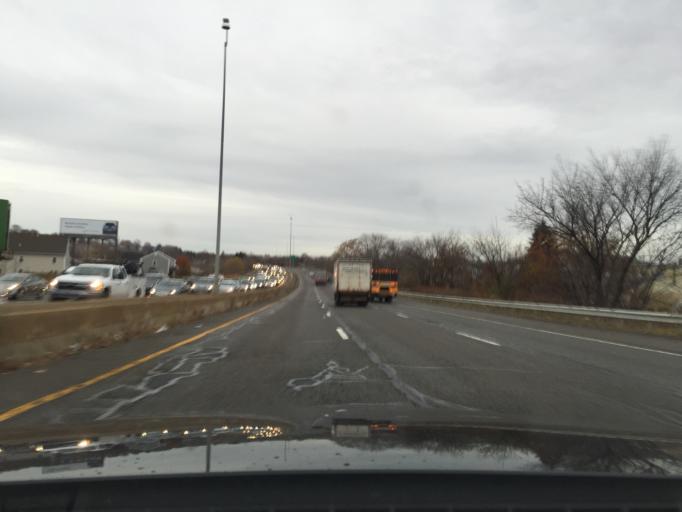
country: US
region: Massachusetts
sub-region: Suffolk County
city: Revere
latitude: 42.4248
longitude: -71.0241
